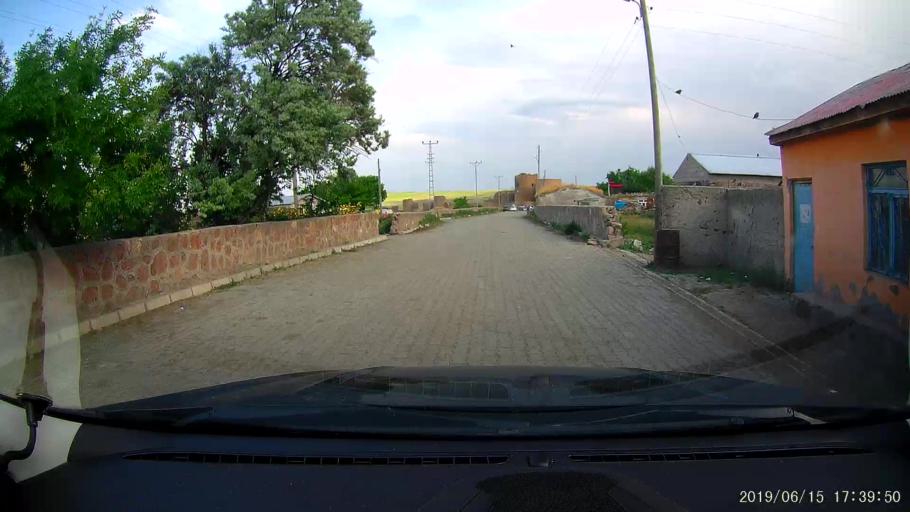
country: TR
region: Kars
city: Basgedikler
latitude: 40.5141
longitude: 43.5714
